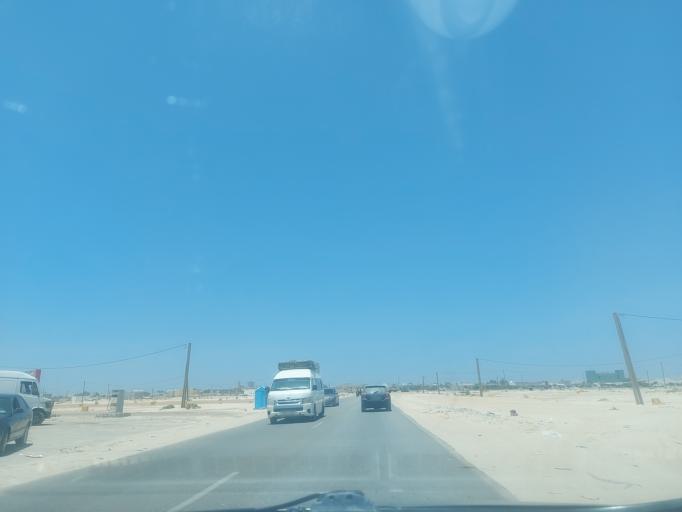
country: MR
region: Nouakchott
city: Nouakchott
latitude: 18.0867
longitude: -15.9537
